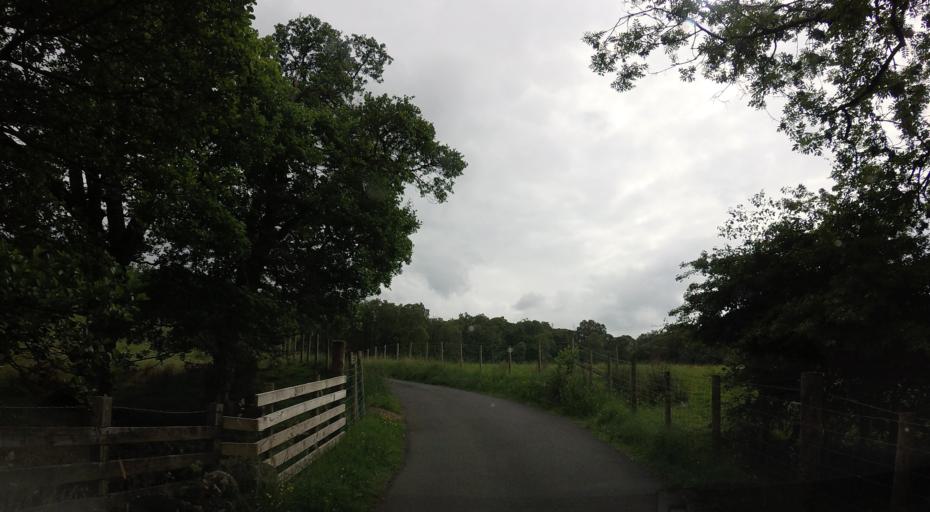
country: GB
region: England
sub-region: Cumbria
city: Keswick
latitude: 54.5639
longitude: -3.1303
